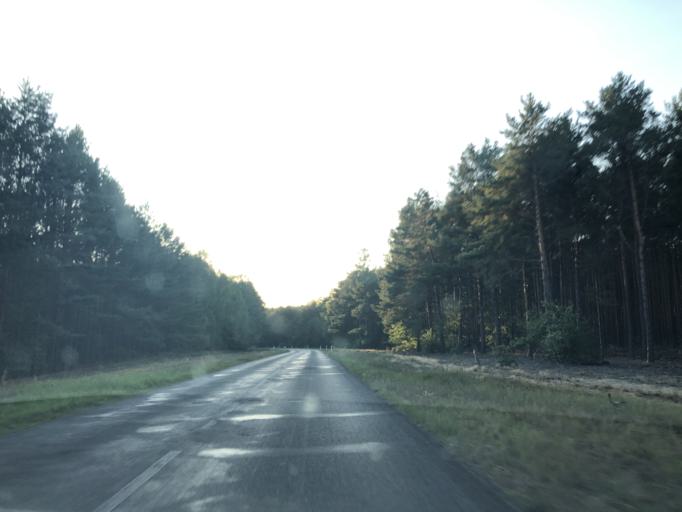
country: DE
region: Brandenburg
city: Mullrose
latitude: 52.2479
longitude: 14.4669
